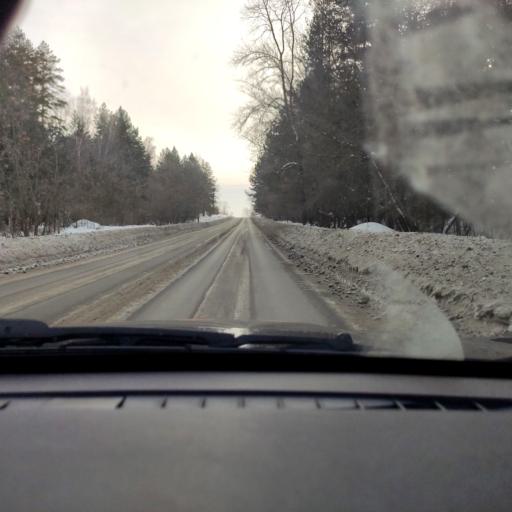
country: RU
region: Samara
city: Pribrezhnyy
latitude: 53.5002
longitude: 49.8488
